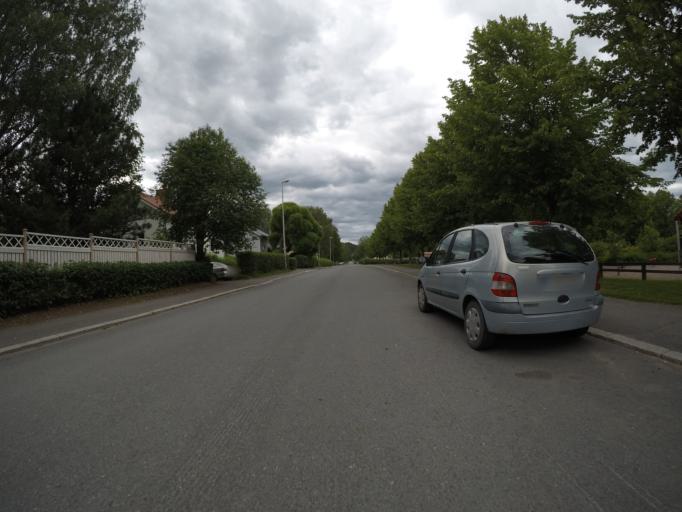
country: FI
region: Haeme
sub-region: Haemeenlinna
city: Haemeenlinna
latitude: 60.9946
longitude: 24.4454
